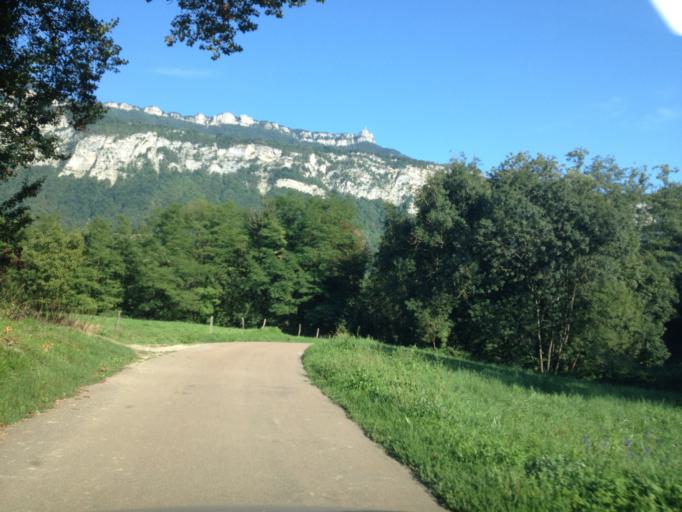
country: FR
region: Rhone-Alpes
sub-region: Departement de la Savoie
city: Sonnaz
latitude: 45.6321
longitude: 5.9203
